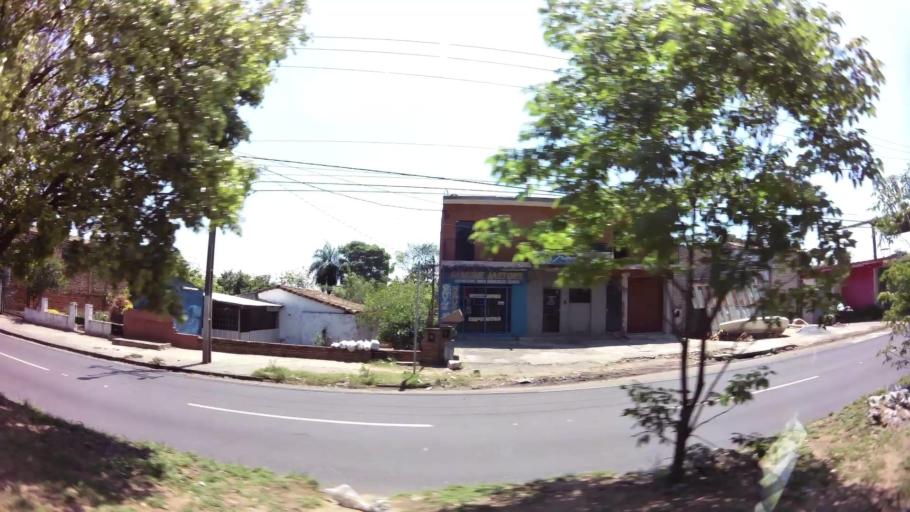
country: PY
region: Central
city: Lambare
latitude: -25.3351
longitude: -57.5796
